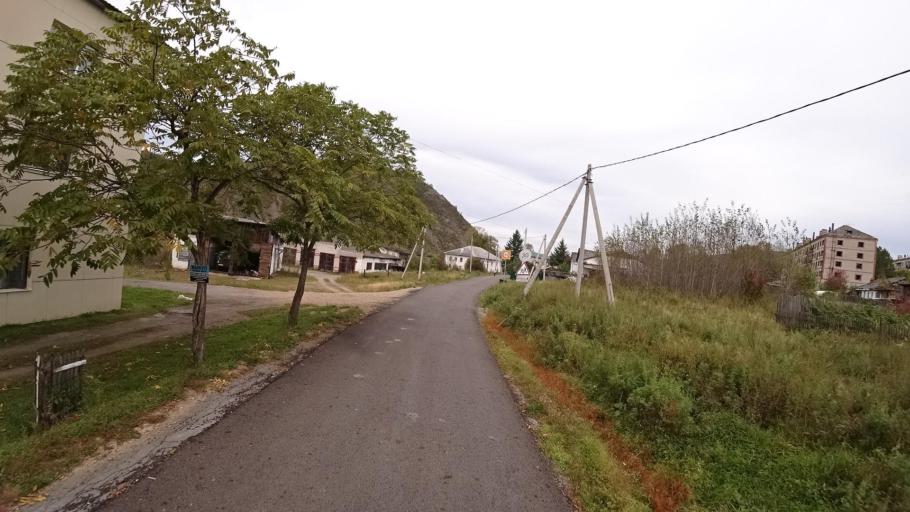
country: RU
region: Jewish Autonomous Oblast
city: Khingansk
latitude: 49.1265
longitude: 131.1903
